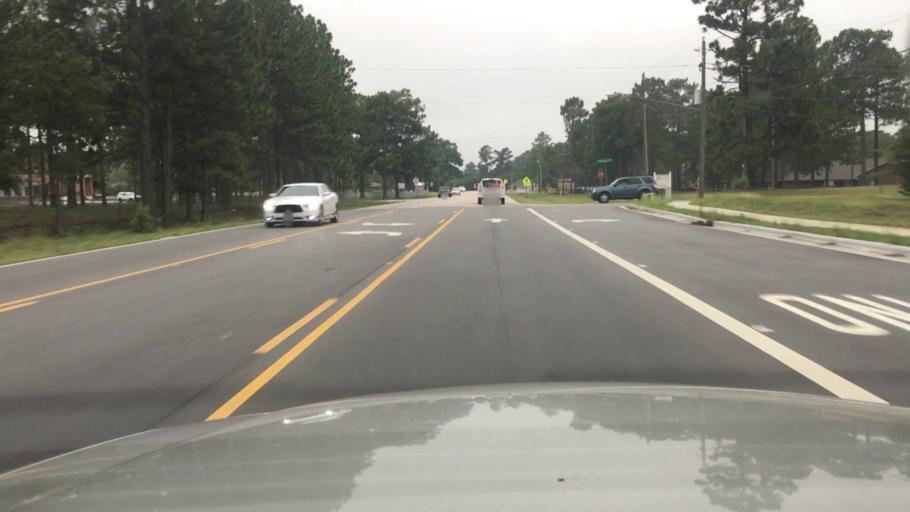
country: US
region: North Carolina
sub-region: Cumberland County
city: Hope Mills
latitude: 34.9808
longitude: -78.9344
